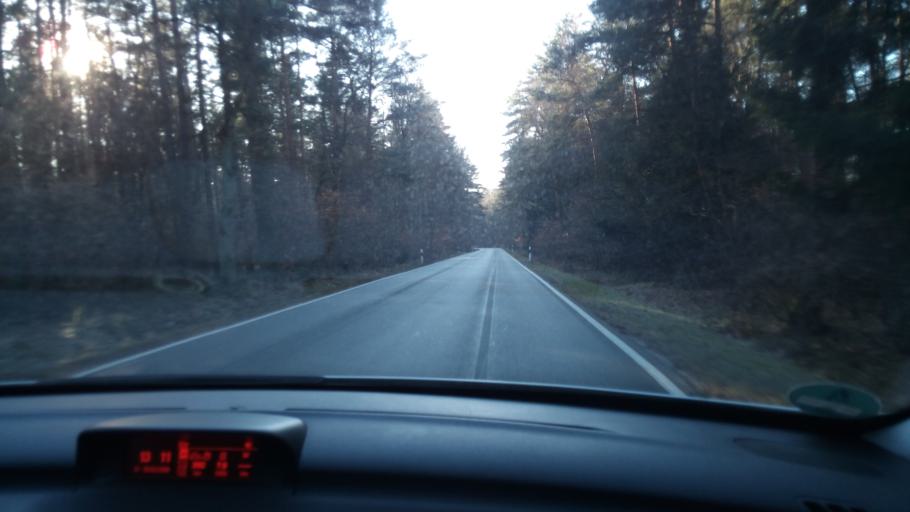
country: DE
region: Schleswig-Holstein
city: Gottin
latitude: 53.5167
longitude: 10.7000
